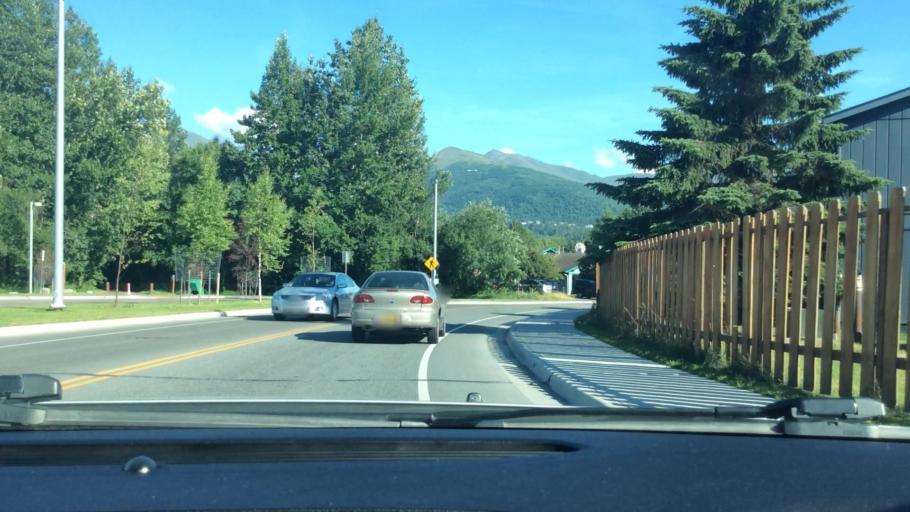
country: US
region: Alaska
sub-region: Anchorage Municipality
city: Elmendorf Air Force Base
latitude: 61.1856
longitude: -149.7317
